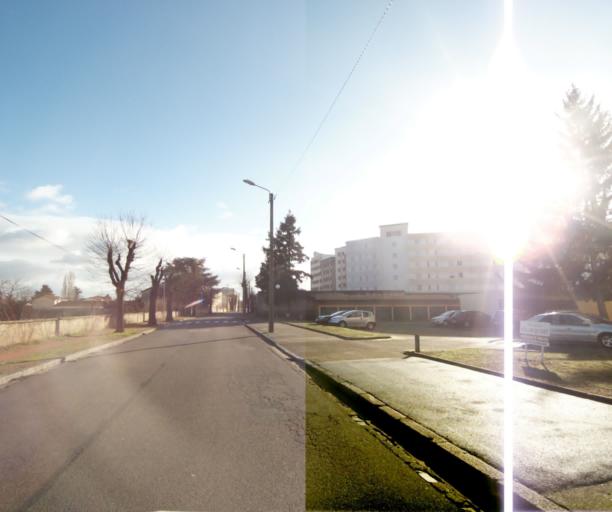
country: FR
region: Rhone-Alpes
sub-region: Departement de la Loire
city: Roanne
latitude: 46.0488
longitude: 4.0769
